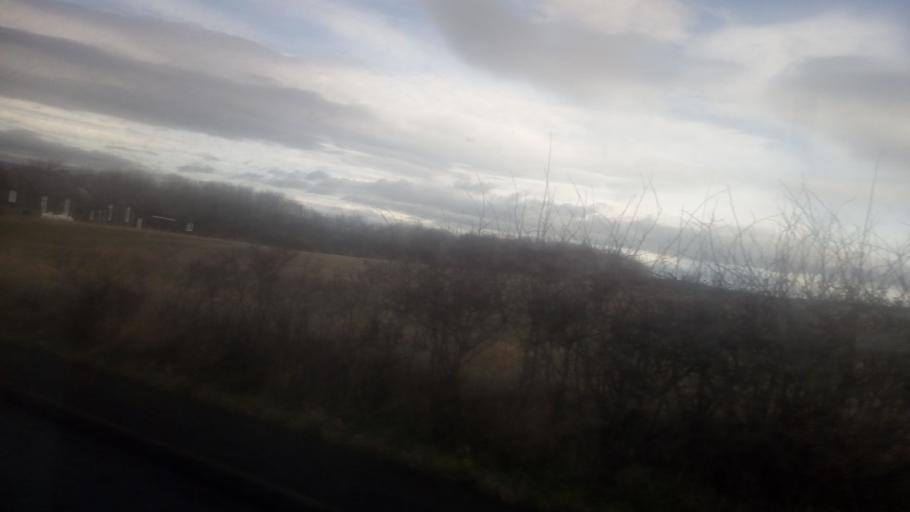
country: GB
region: Scotland
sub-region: Midlothian
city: Dalkeith
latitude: 55.8883
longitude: -3.0381
